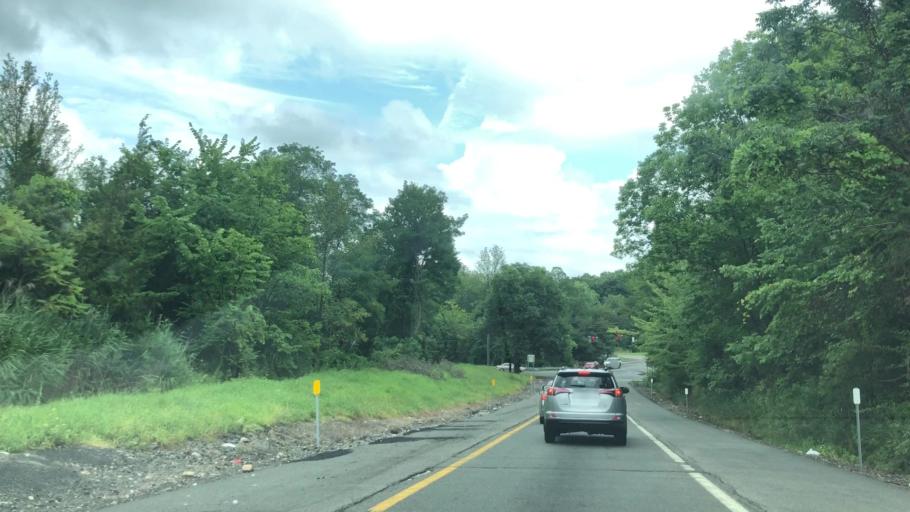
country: US
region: New York
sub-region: Rockland County
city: Spring Valley
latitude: 41.0994
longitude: -74.0344
